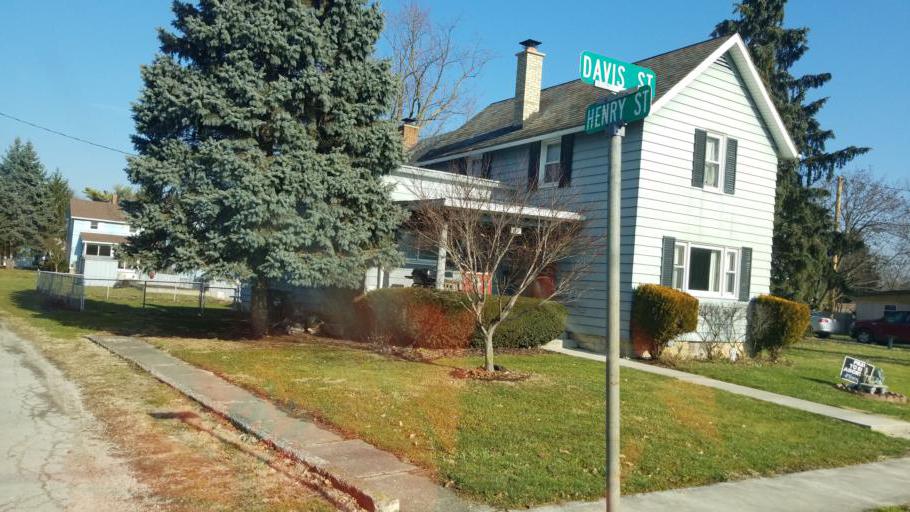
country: US
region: Ohio
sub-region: Seneca County
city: Tiffin
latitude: 41.1263
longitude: -83.1710
